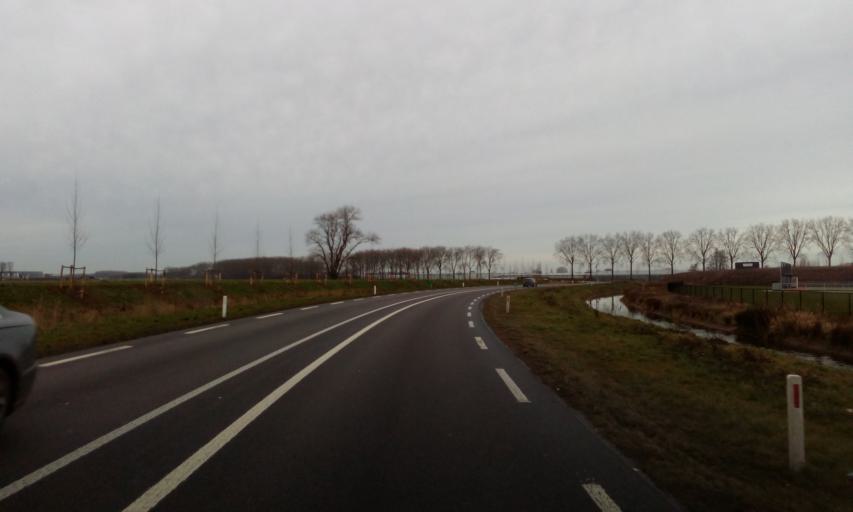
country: NL
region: Gelderland
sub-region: Gemeente Zaltbommel
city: Zaltbommel
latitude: 51.7961
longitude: 5.2377
